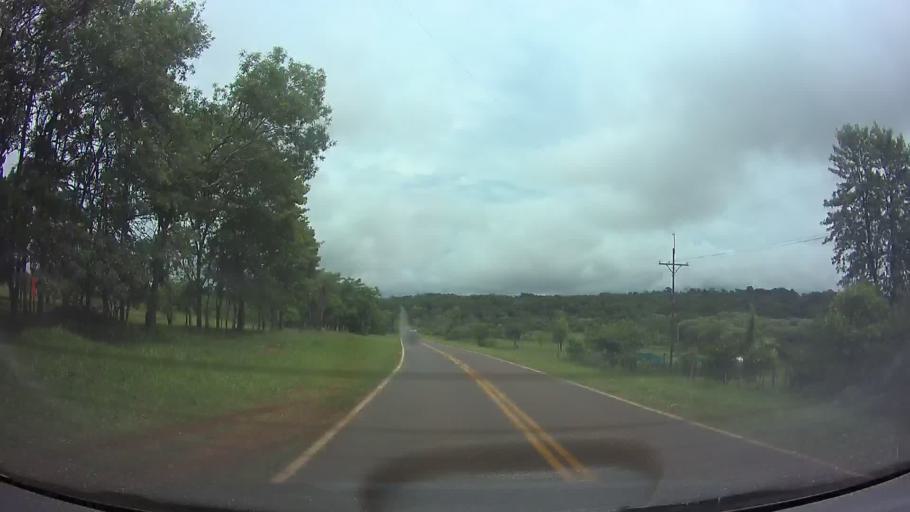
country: PY
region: Paraguari
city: Ybycui
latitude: -25.9732
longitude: -57.0762
